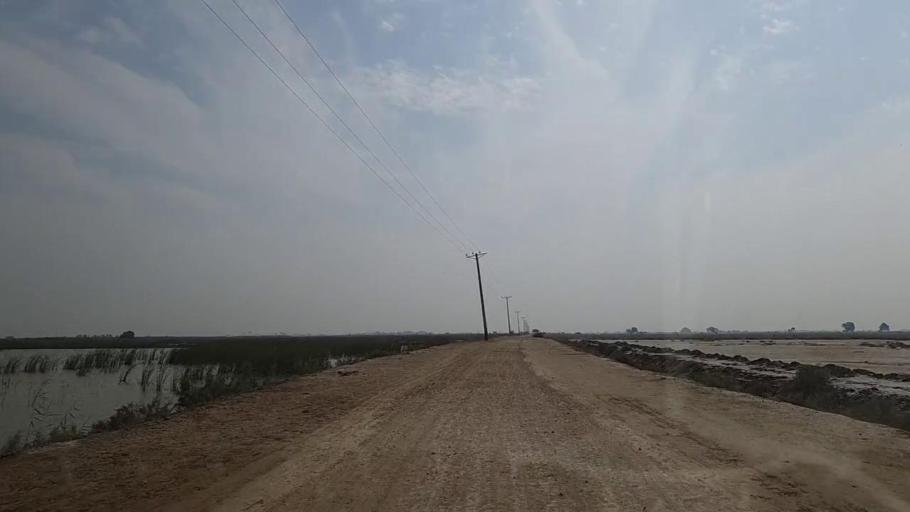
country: PK
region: Sindh
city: Mirpur Batoro
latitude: 24.6080
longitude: 68.2093
